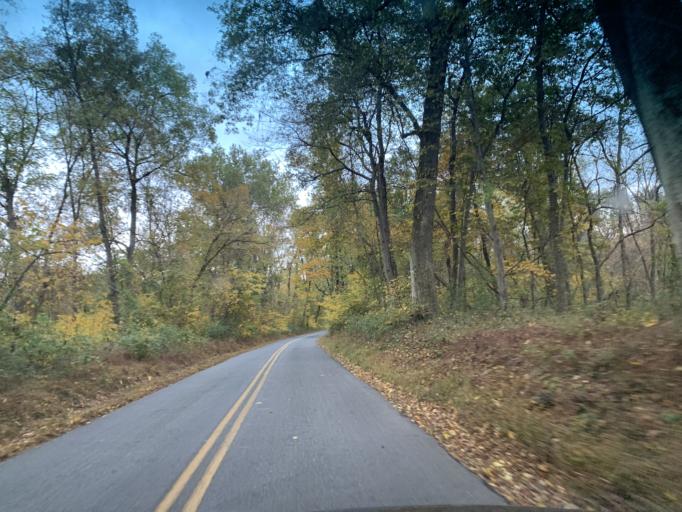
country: US
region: Maryland
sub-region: Harford County
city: Havre de Grace
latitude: 39.6223
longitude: -76.1579
